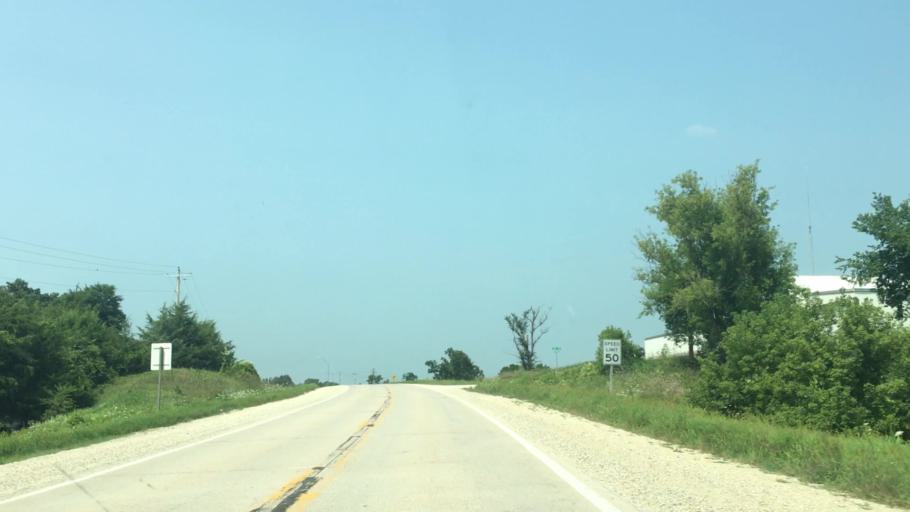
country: US
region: Iowa
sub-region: Fayette County
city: West Union
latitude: 43.1156
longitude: -91.8692
